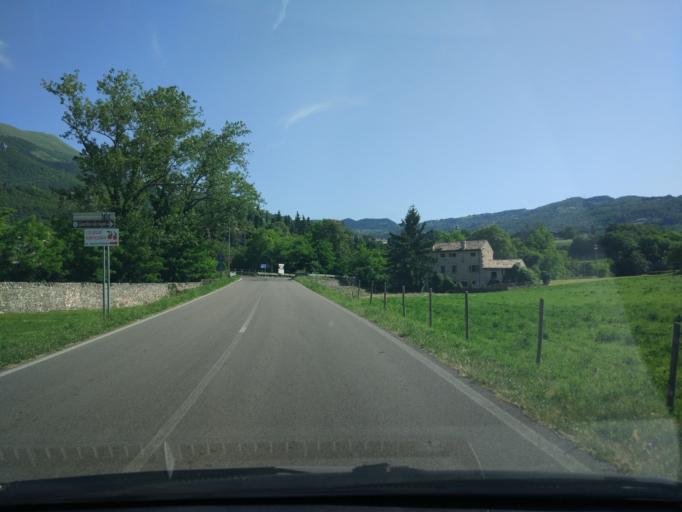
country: IT
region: Veneto
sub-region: Provincia di Verona
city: Caprino Veronese
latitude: 45.6085
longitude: 10.8169
